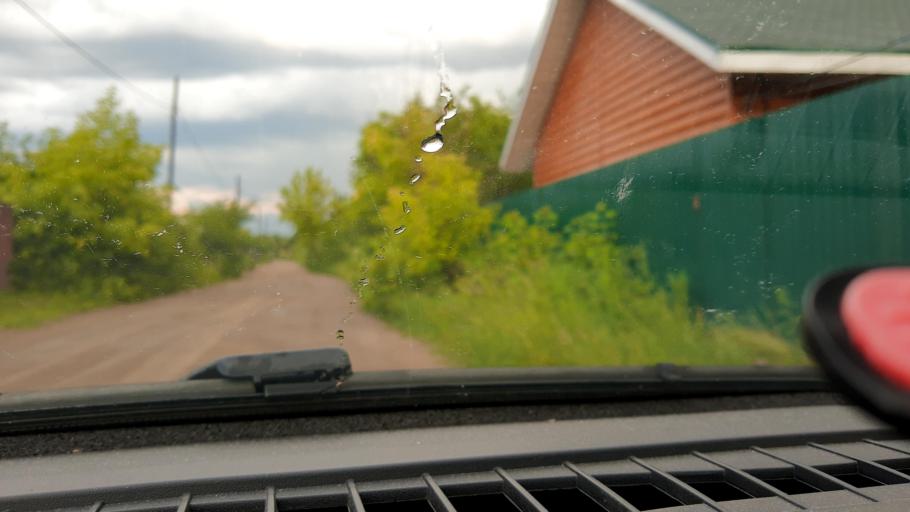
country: RU
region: Nizjnij Novgorod
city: Zavolzh'ye
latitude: 56.6590
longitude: 43.4261
